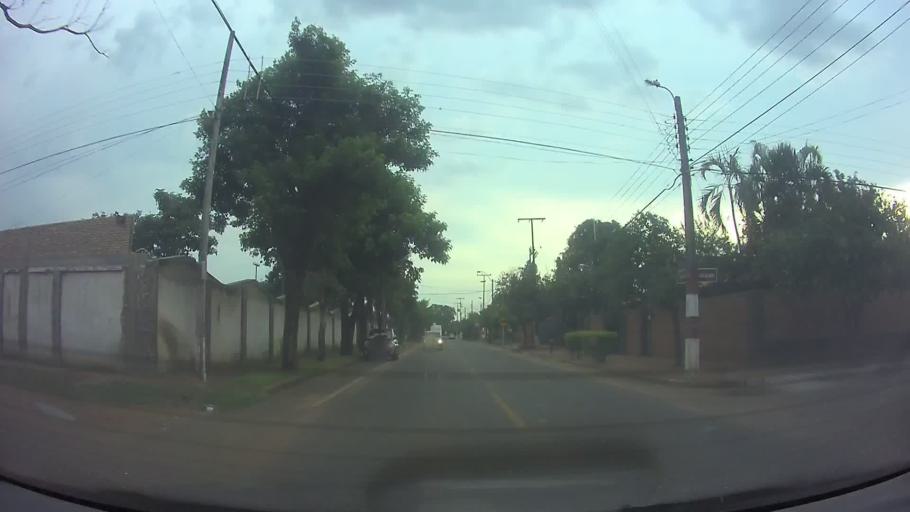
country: PY
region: Central
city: San Lorenzo
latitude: -25.2742
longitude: -57.4776
